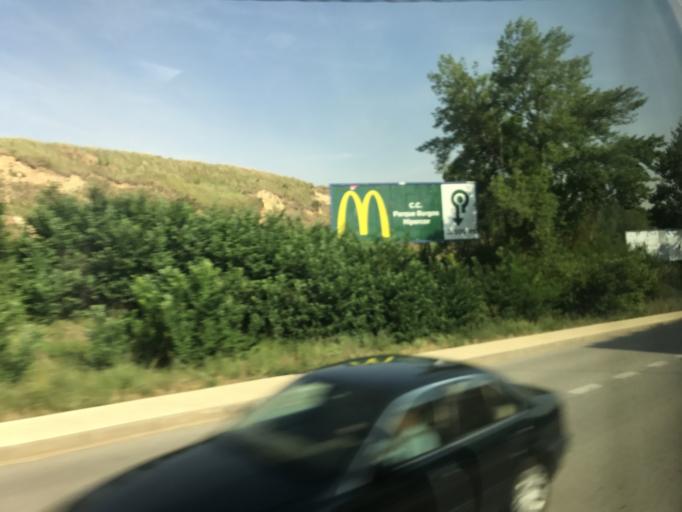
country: ES
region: Castille and Leon
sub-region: Provincia de Burgos
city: Burgos
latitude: 42.3252
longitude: -3.7013
